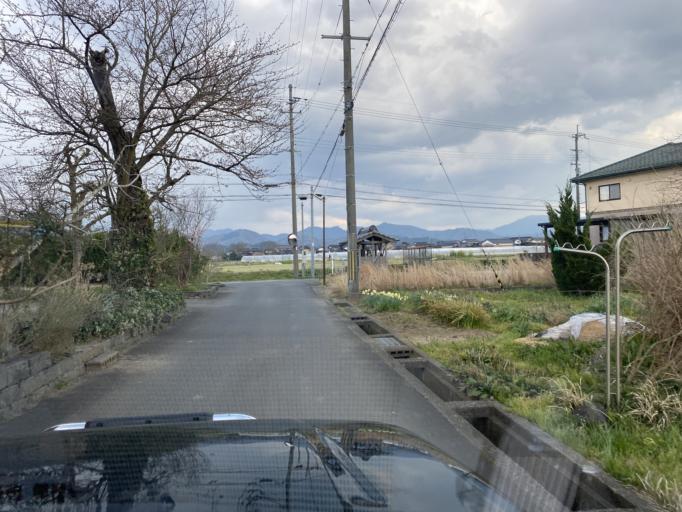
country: JP
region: Hyogo
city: Toyooka
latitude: 35.5212
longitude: 134.8264
